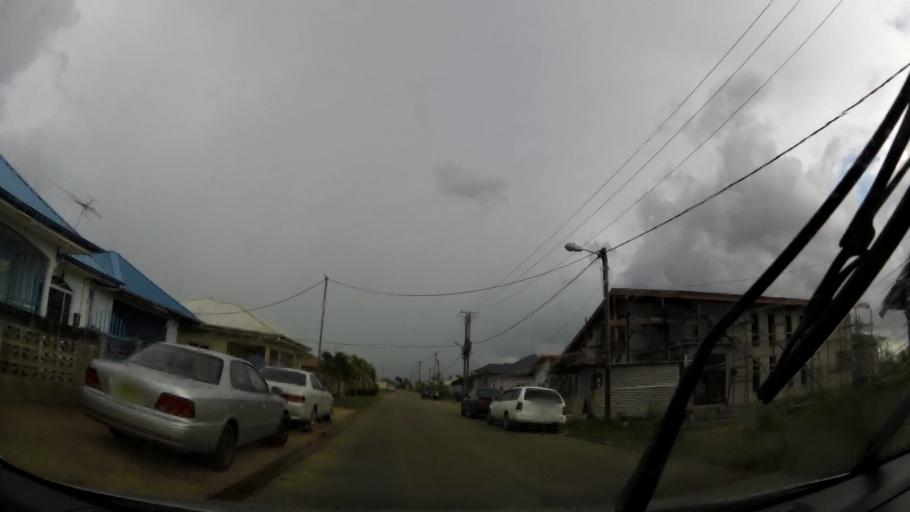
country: SR
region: Commewijne
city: Nieuw Amsterdam
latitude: 5.8514
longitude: -55.1140
